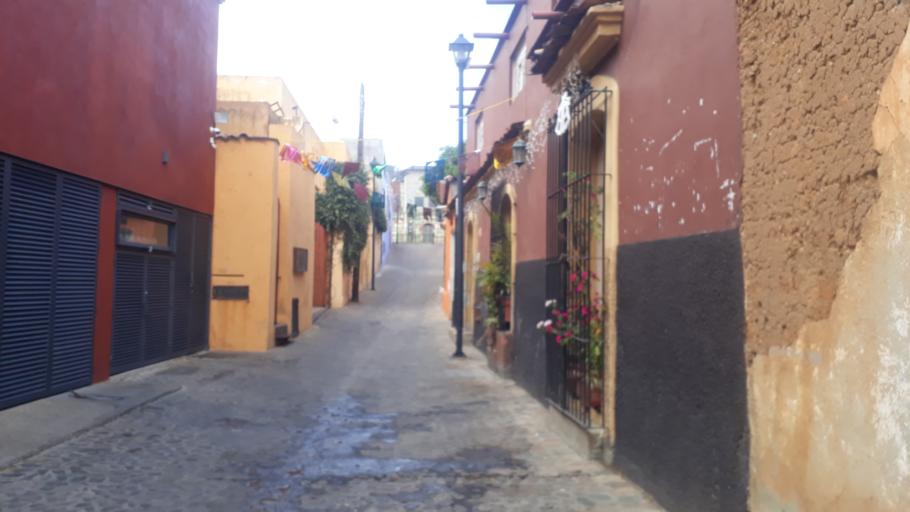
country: MX
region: Oaxaca
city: Oaxaca de Juarez
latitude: 17.0716
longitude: -96.7231
